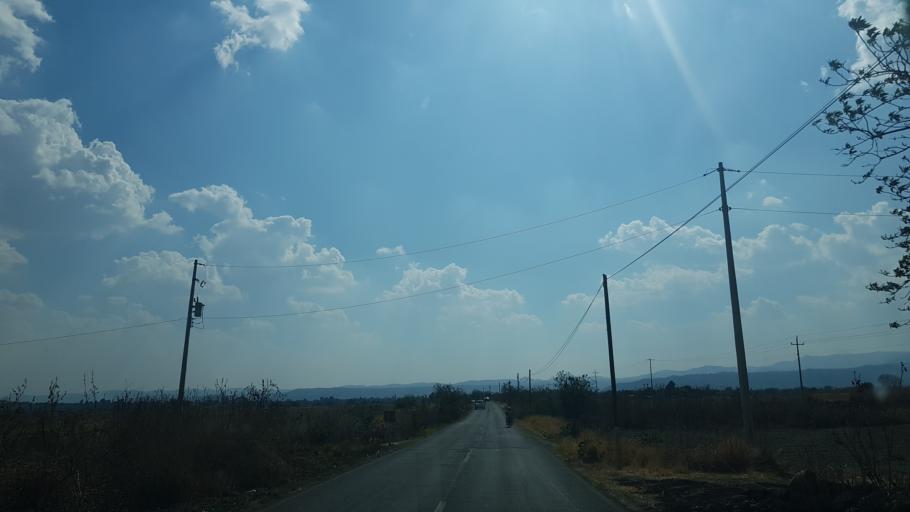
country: MX
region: Puebla
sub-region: Atlixco
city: Colonia Agricola de Ocotepec (Colonia San Jose)
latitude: 18.8992
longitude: -98.4979
